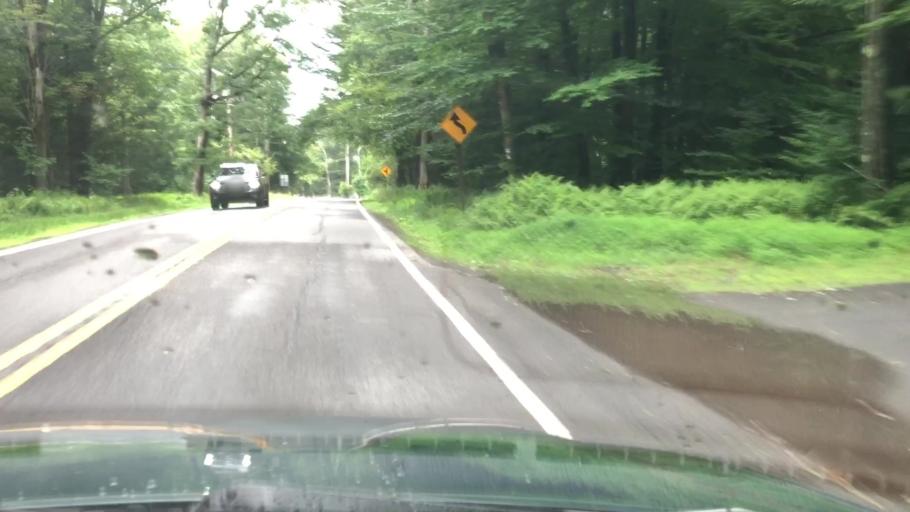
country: US
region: Pennsylvania
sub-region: Monroe County
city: Mountainhome
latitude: 41.3079
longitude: -75.2109
